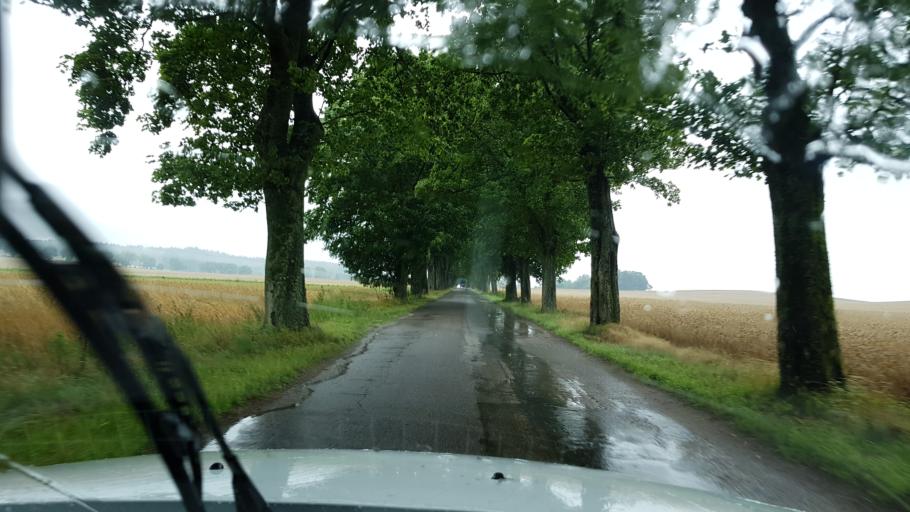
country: PL
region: West Pomeranian Voivodeship
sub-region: Powiat gryficki
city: Brojce
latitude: 53.9417
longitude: 15.4215
